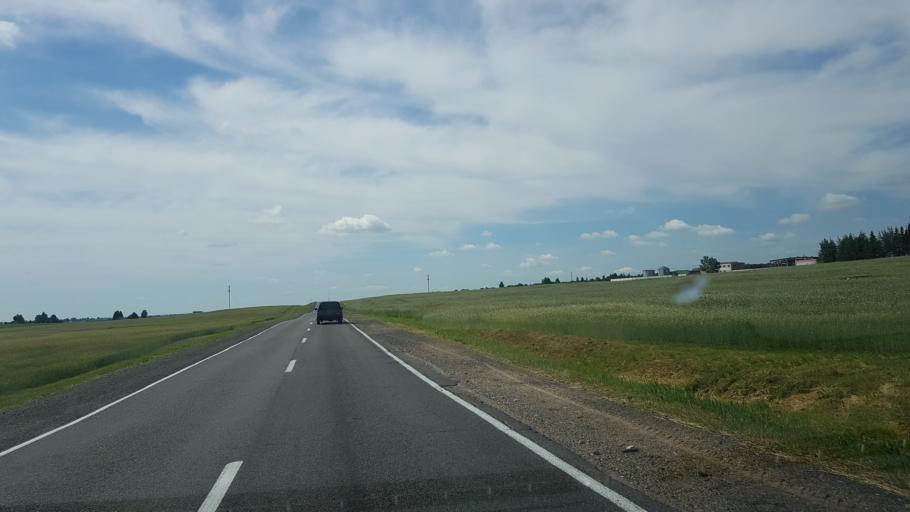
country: BY
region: Vitebsk
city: Dubrowna
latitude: 54.6484
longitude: 30.6659
